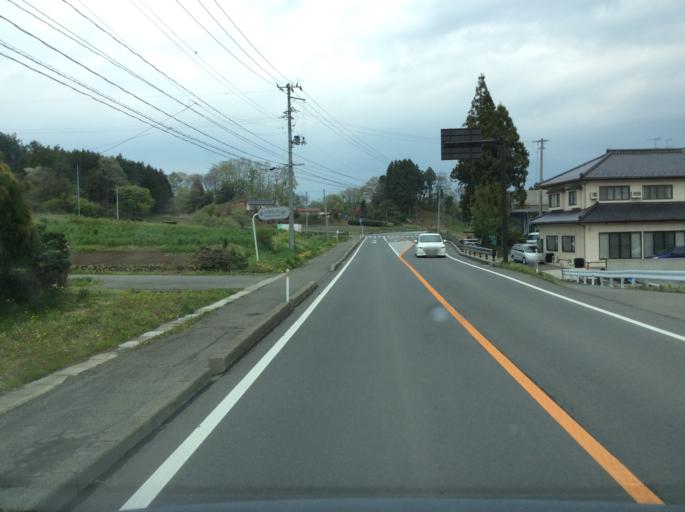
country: JP
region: Fukushima
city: Funehikimachi-funehiki
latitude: 37.3571
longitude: 140.6048
